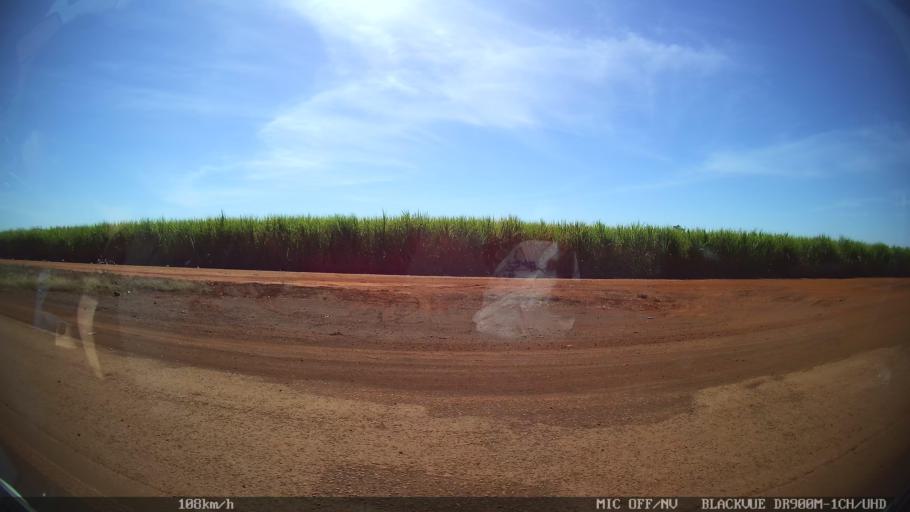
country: BR
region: Sao Paulo
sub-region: Guaira
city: Guaira
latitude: -20.4435
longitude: -48.3386
